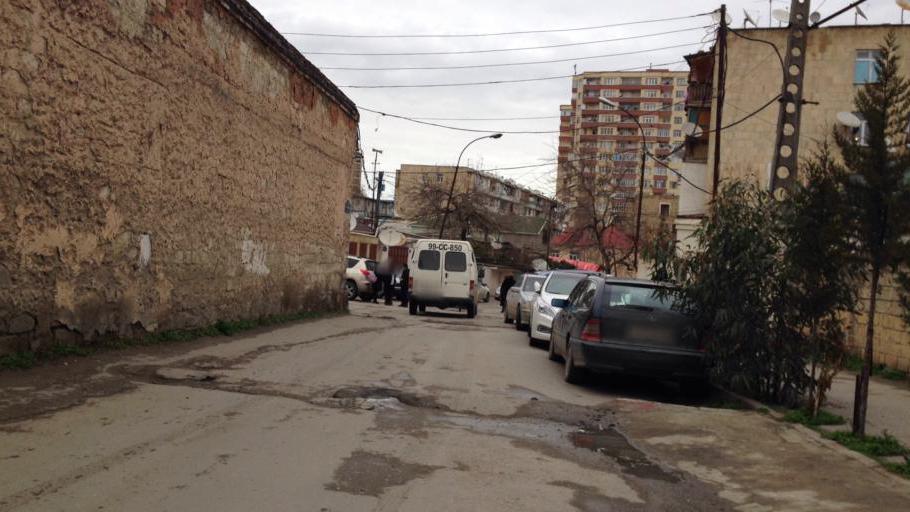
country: AZ
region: Baki
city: Baku
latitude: 40.3885
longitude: 49.8513
